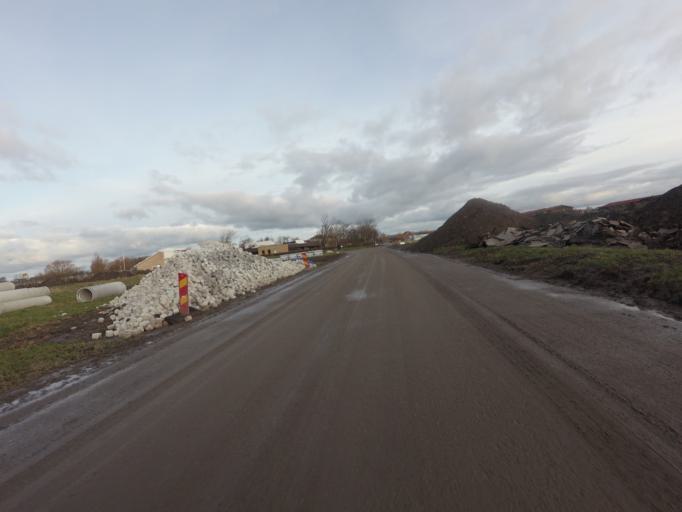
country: SE
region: Skane
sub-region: Hoganas Kommun
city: Hoganas
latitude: 56.1909
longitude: 12.5693
